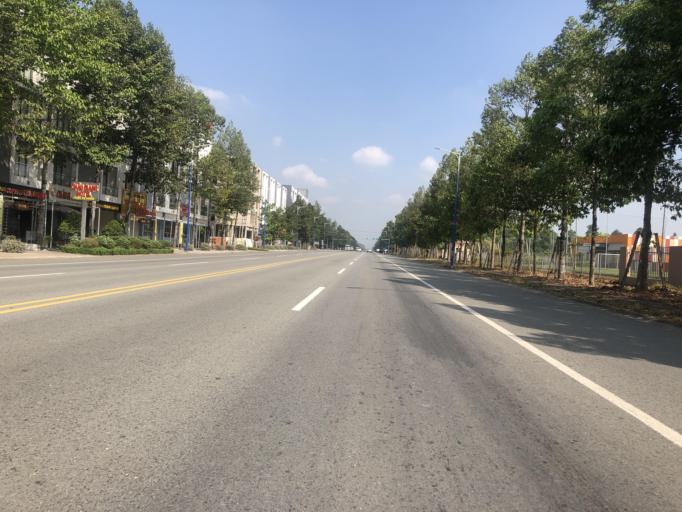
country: VN
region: Binh Duong
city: Thu Dau Mot
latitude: 11.0690
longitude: 106.6767
